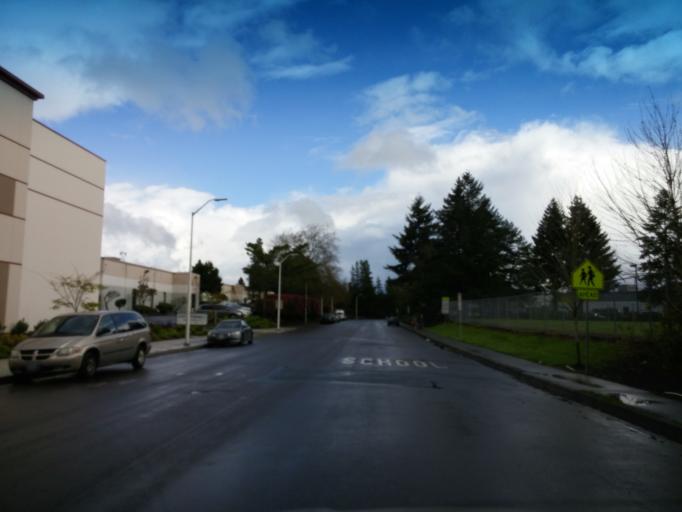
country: US
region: Oregon
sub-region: Washington County
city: Aloha
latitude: 45.5075
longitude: -122.8493
